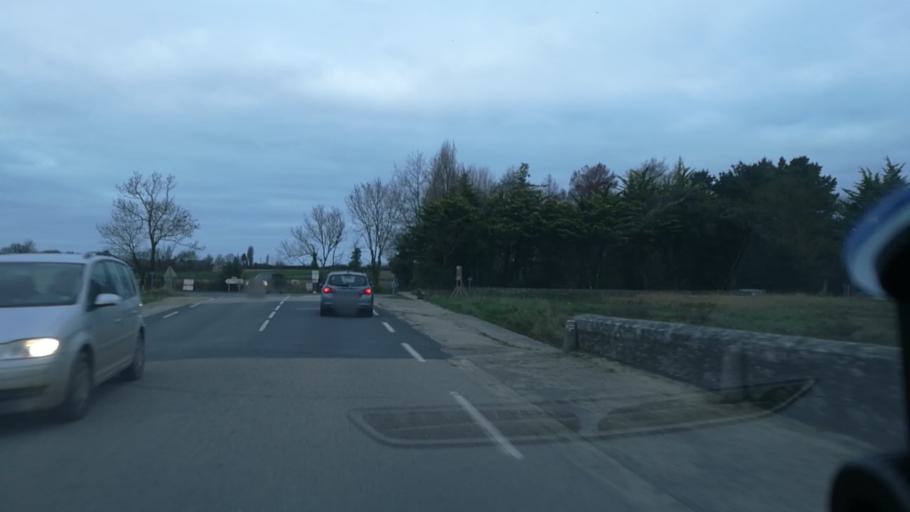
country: FR
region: Lower Normandy
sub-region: Departement de la Manche
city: Reville
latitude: 49.6124
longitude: -1.2560
